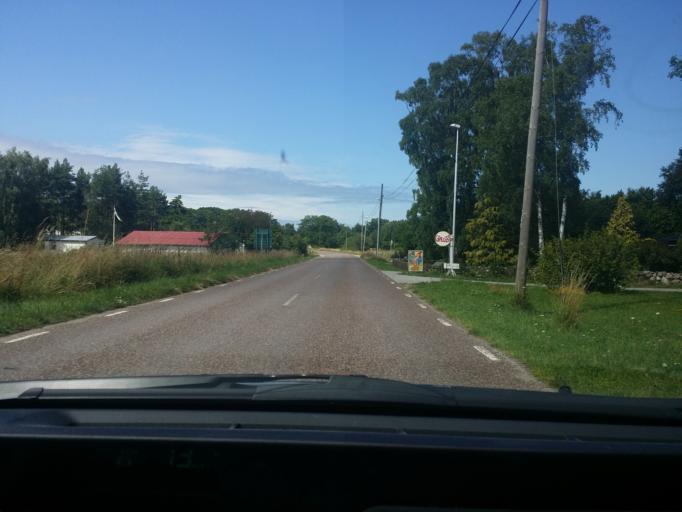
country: SE
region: Kalmar
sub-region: Borgholms Kommun
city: Borgholm
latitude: 57.2088
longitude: 16.9747
